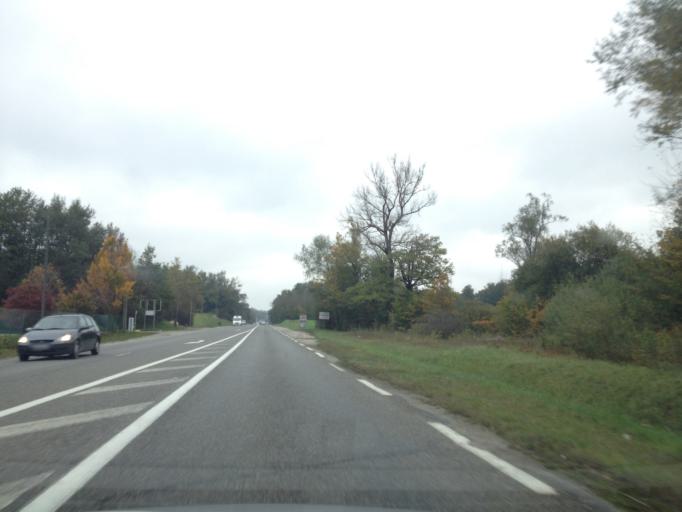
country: FR
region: Rhone-Alpes
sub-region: Departement de la Haute-Savoie
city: Seynod
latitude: 45.8539
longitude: 6.0633
